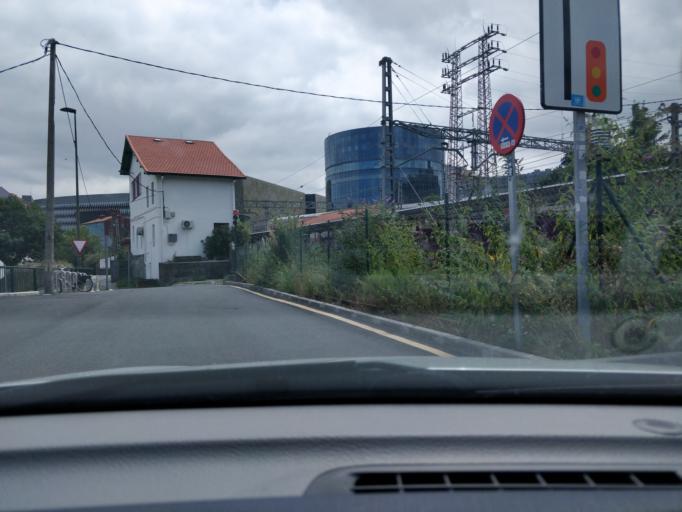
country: ES
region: Basque Country
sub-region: Bizkaia
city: Bilbao
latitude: 43.2644
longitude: -2.9560
